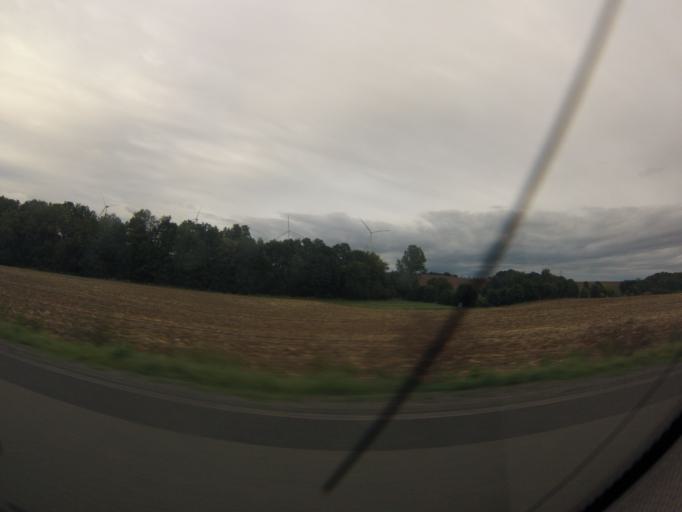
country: DE
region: Thuringia
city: Wildenborten
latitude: 50.8979
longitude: 12.2941
